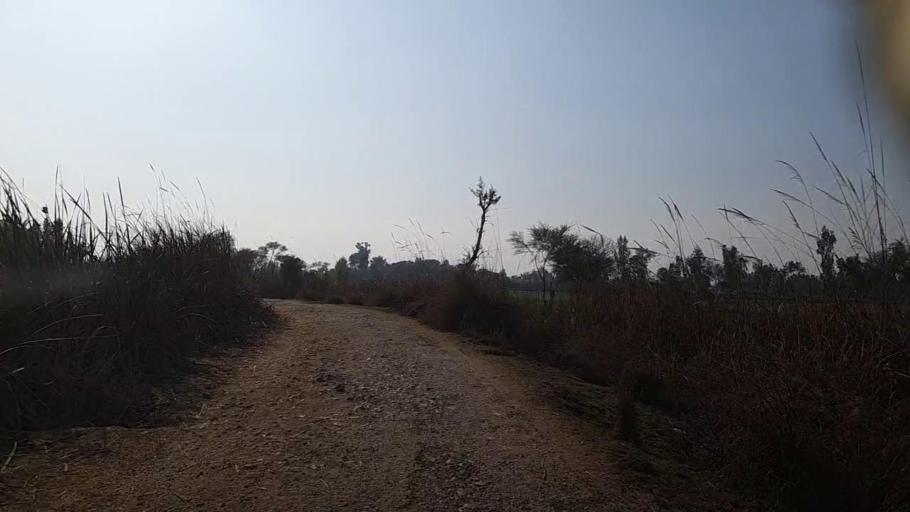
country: PK
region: Sindh
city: Mirpur Mathelo
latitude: 27.9020
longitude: 69.6081
